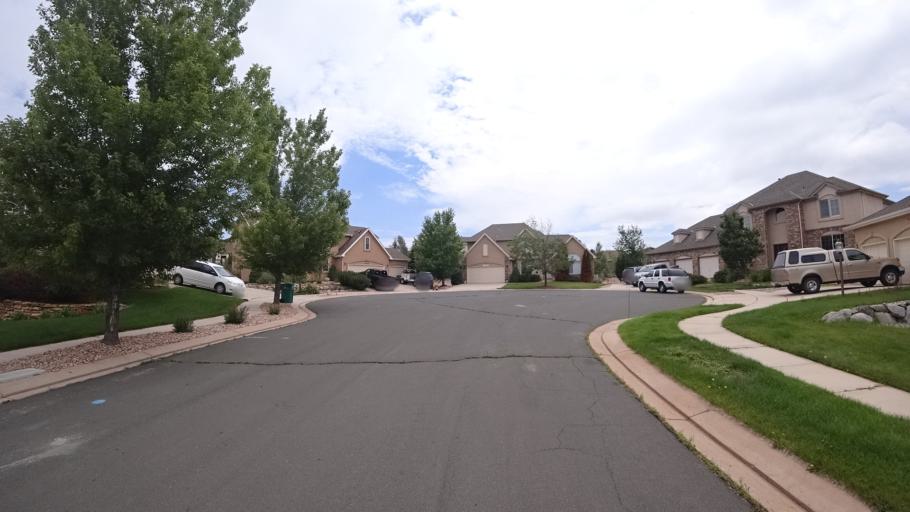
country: US
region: Colorado
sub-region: El Paso County
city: Gleneagle
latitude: 39.0156
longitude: -104.8050
